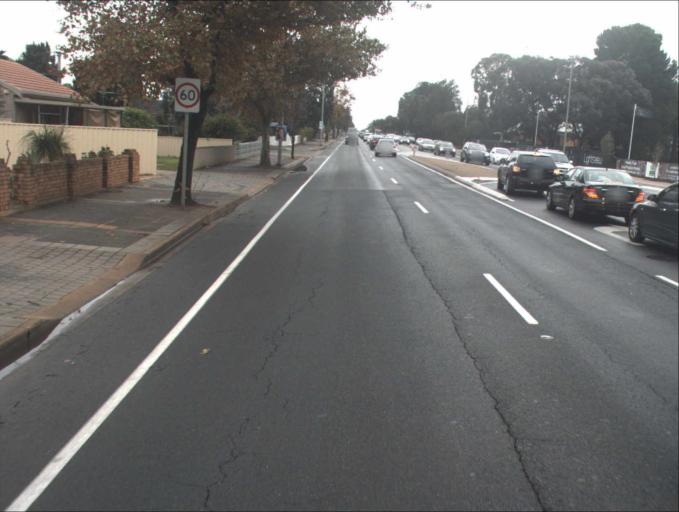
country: AU
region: South Australia
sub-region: Port Adelaide Enfield
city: Enfield
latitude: -34.8635
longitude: 138.6185
